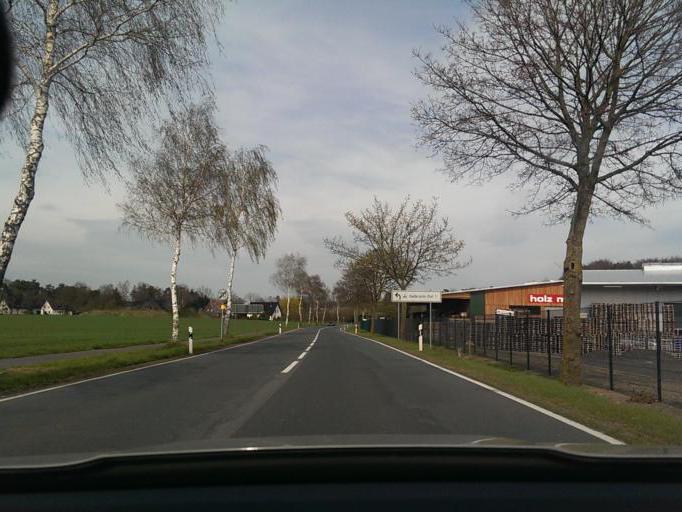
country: DE
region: North Rhine-Westphalia
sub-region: Regierungsbezirk Detmold
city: Delbruck
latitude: 51.7742
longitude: 8.5858
